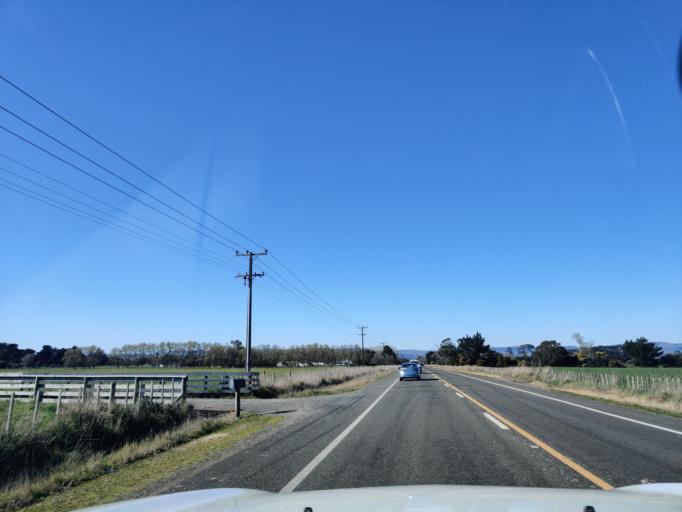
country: NZ
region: Manawatu-Wanganui
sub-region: Palmerston North City
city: Palmerston North
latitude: -40.3006
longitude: 175.5792
